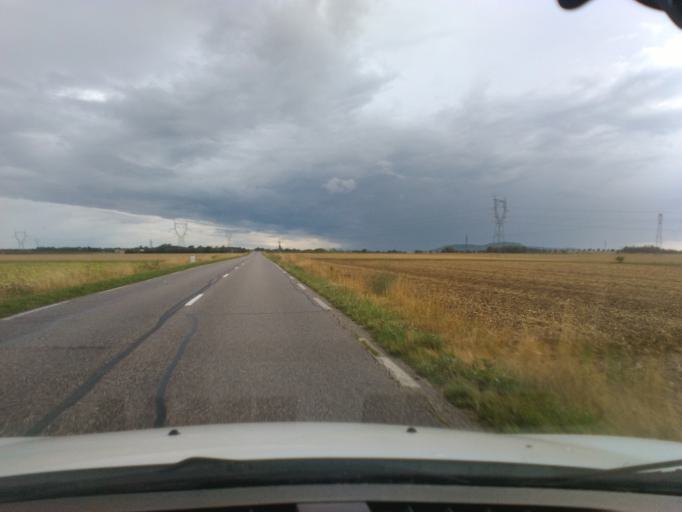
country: FR
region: Lorraine
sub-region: Departement de Meurthe-et-Moselle
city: Vezelise
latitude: 48.4855
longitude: 6.1436
